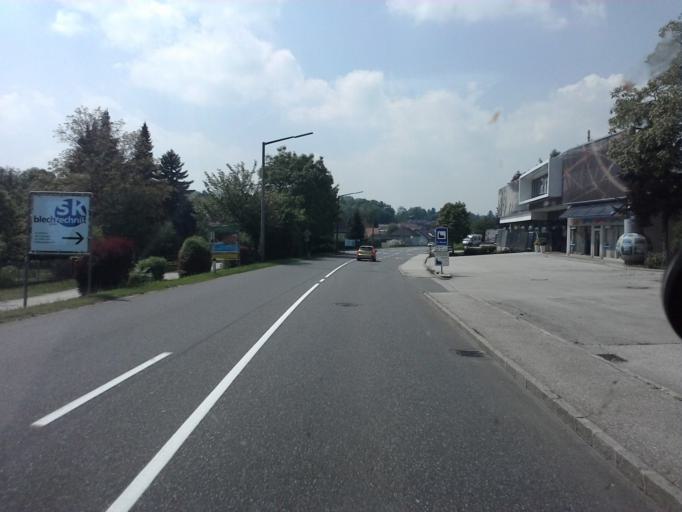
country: AT
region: Upper Austria
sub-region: Politischer Bezirk Steyr-Land
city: Bad Hall
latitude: 48.0301
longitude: 14.2209
